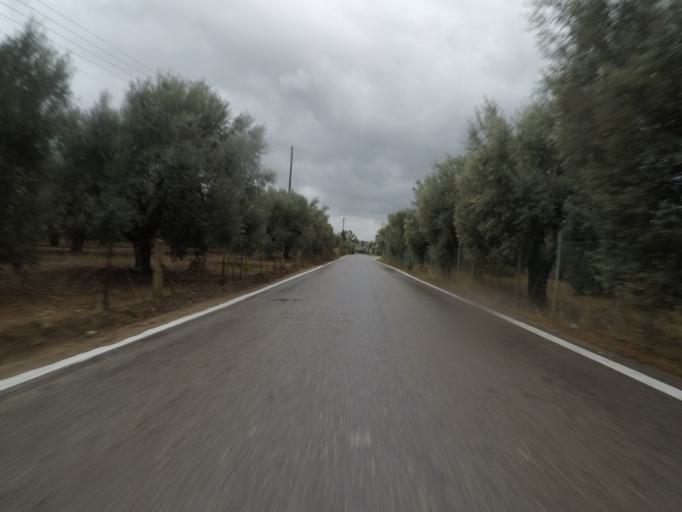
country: GR
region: Peloponnese
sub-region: Nomos Messinias
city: Khora
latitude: 36.9881
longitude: 21.6787
